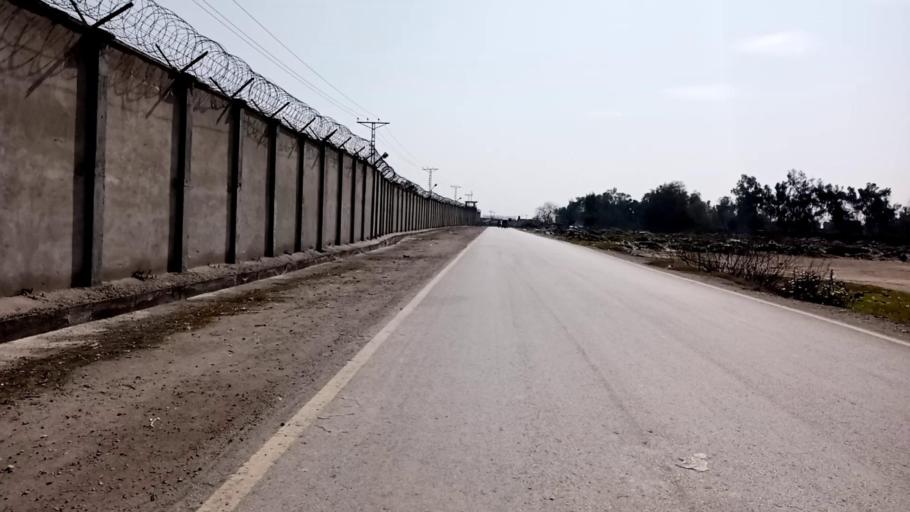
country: PK
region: Khyber Pakhtunkhwa
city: Peshawar
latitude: 33.9892
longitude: 71.5121
